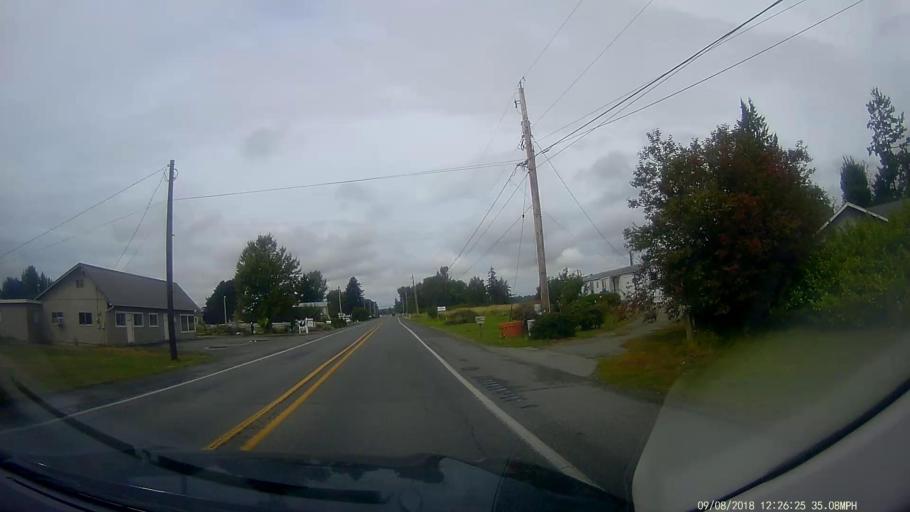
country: US
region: Washington
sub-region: Skagit County
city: Mount Vernon
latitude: 48.4371
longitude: -122.3800
